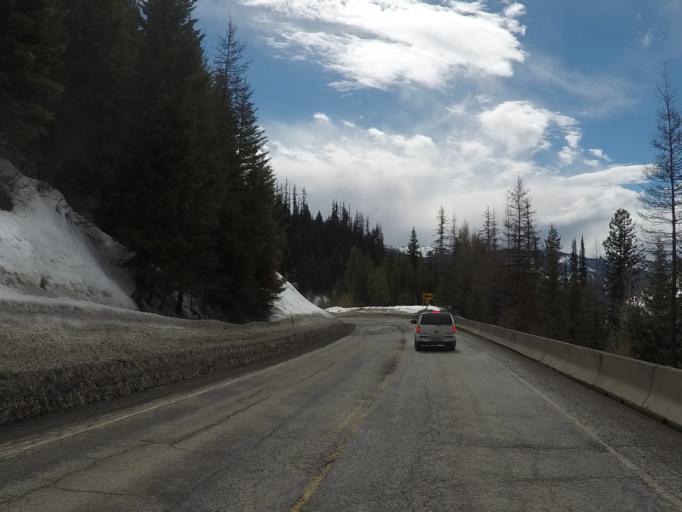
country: US
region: Montana
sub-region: Ravalli County
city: Stevensville
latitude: 46.6171
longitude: -114.5904
